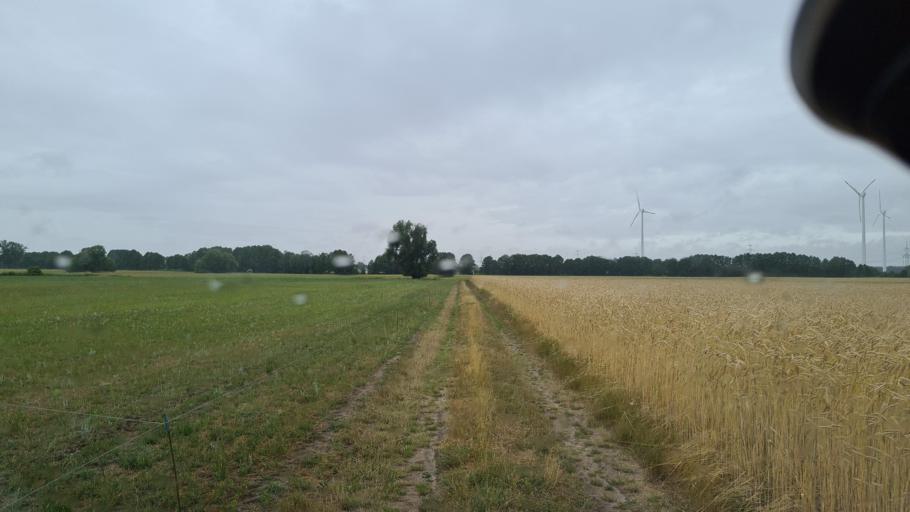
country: DE
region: Saxony-Anhalt
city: Holzdorf
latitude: 51.8202
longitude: 13.1550
